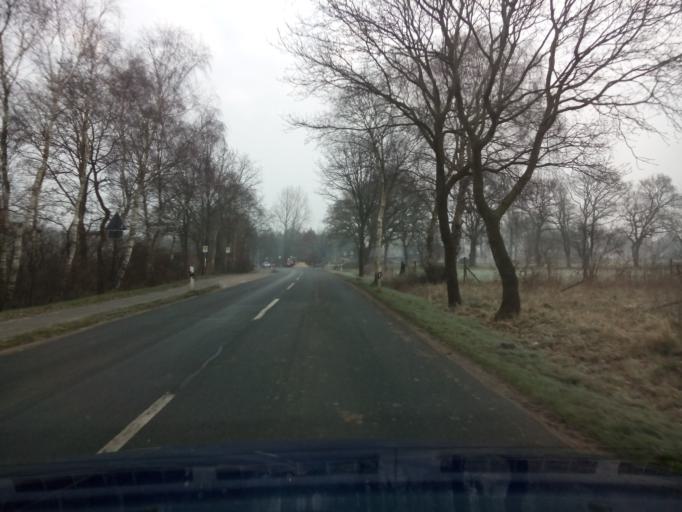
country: DE
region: Lower Saxony
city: Schiffdorf
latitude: 53.5884
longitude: 8.6548
